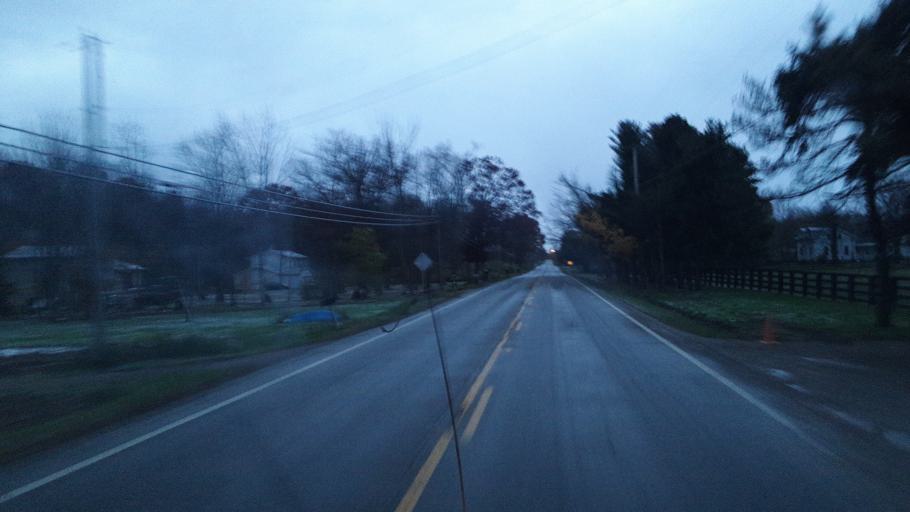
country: US
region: Ohio
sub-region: Portage County
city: Mantua
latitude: 41.3352
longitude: -81.2215
